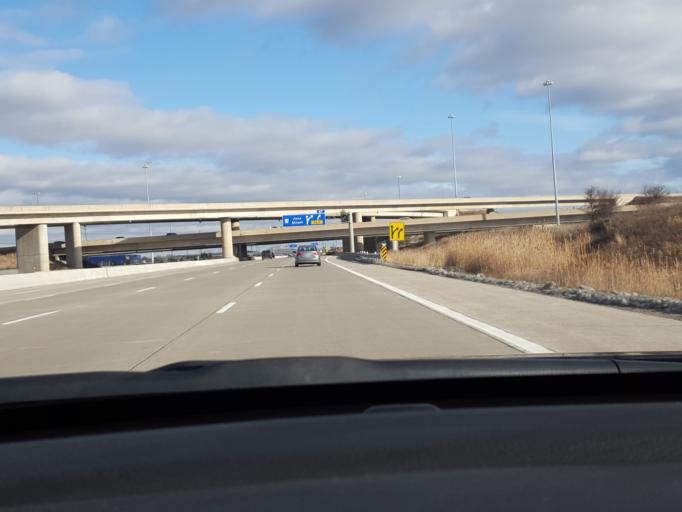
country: CA
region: Ontario
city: Concord
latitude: 43.7823
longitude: -79.5407
